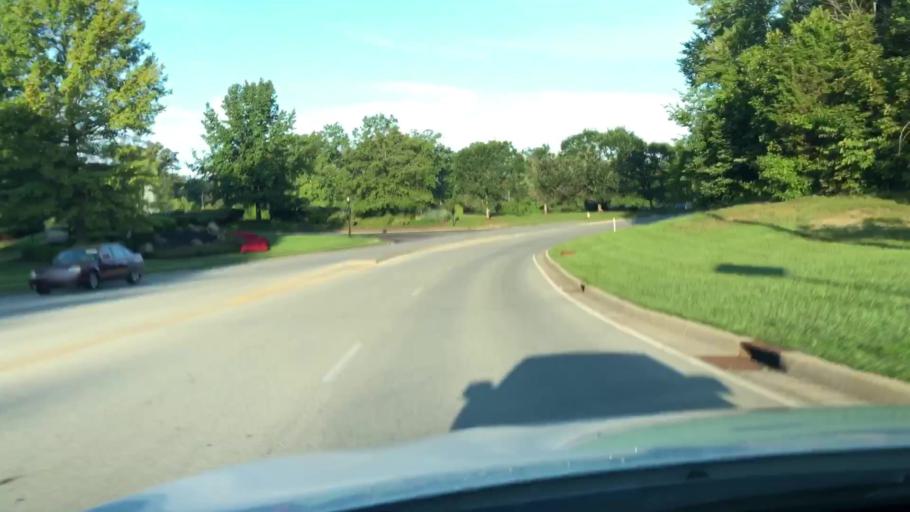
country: US
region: Kentucky
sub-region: Jefferson County
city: Middletown
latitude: 38.2166
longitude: -85.5315
